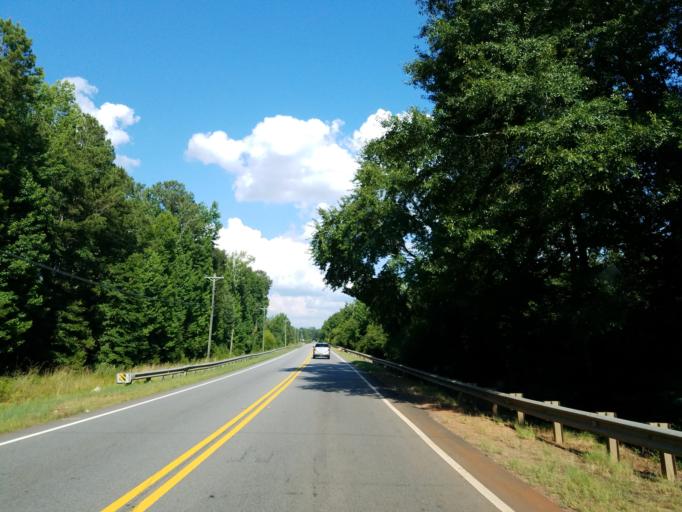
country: US
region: Georgia
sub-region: Houston County
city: Perry
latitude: 32.5491
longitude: -83.7671
